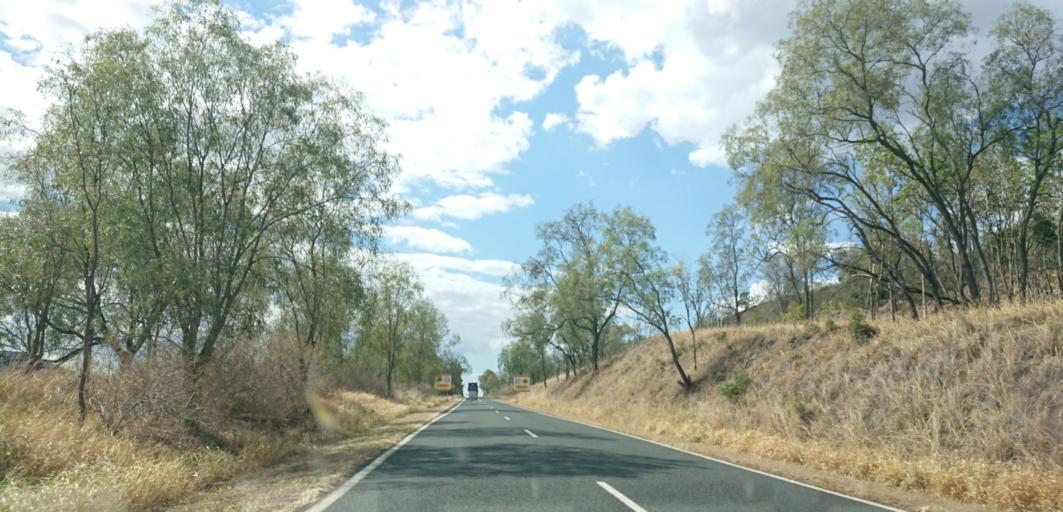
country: AU
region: Queensland
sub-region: Lockyer Valley
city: Gatton
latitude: -27.6841
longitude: 152.1480
